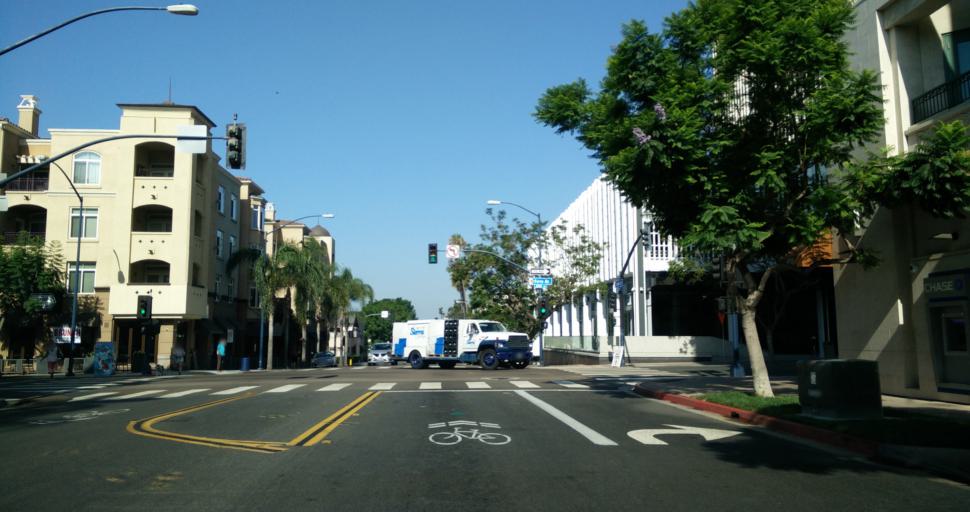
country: US
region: California
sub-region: San Diego County
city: San Diego
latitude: 32.7314
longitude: -117.1599
